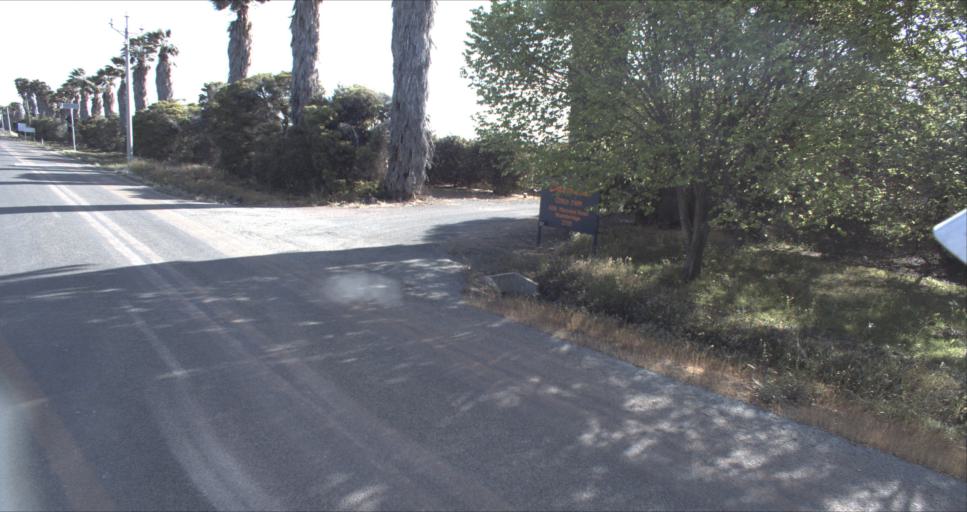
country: AU
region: New South Wales
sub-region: Leeton
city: Leeton
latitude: -34.5211
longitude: 146.2833
